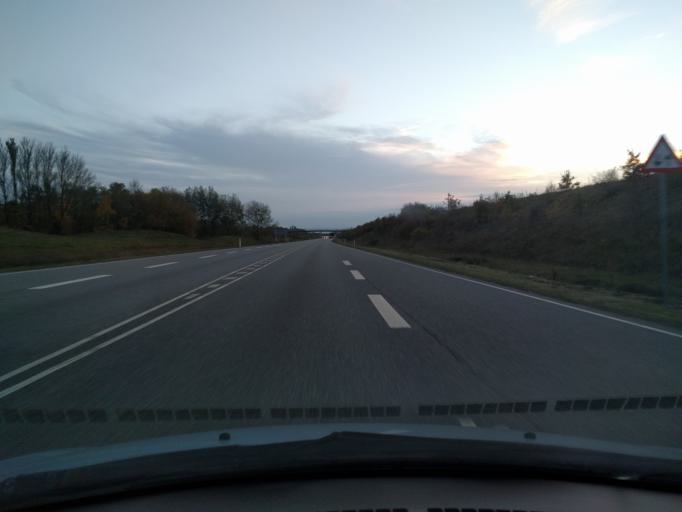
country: DK
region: South Denmark
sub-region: Odense Kommune
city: Neder Holluf
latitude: 55.3725
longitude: 10.4757
